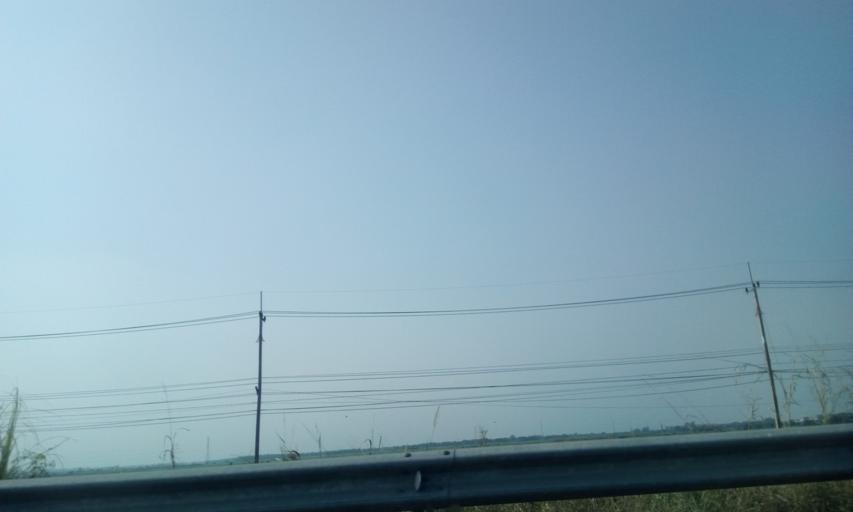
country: TH
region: Sing Buri
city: Phrom Buri
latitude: 14.7852
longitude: 100.4358
